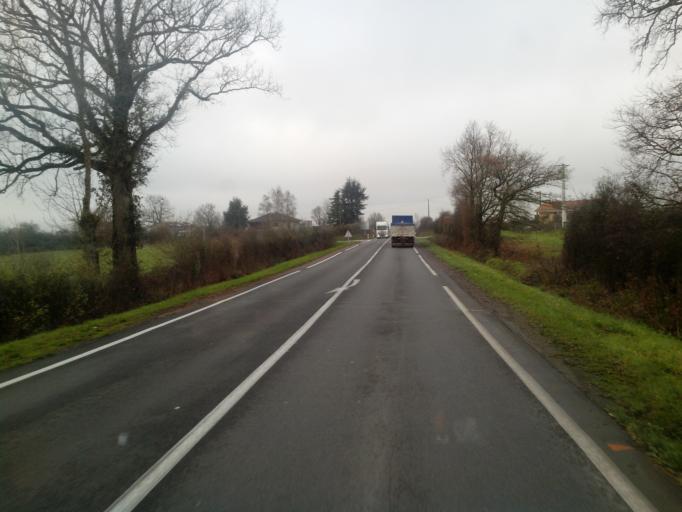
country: FR
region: Poitou-Charentes
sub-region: Departement des Deux-Sevres
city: Viennay
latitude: 46.6722
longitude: -0.2576
